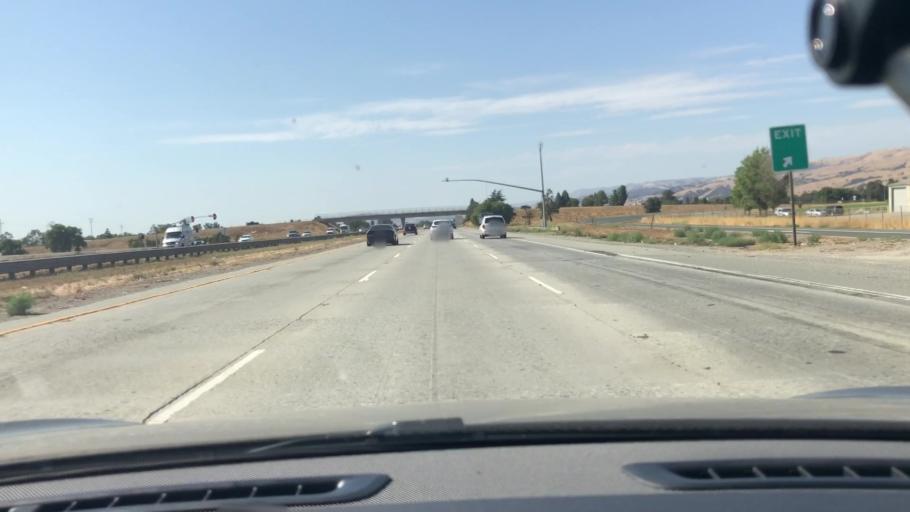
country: US
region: California
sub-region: Santa Clara County
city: San Martin
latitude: 37.0558
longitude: -121.5824
